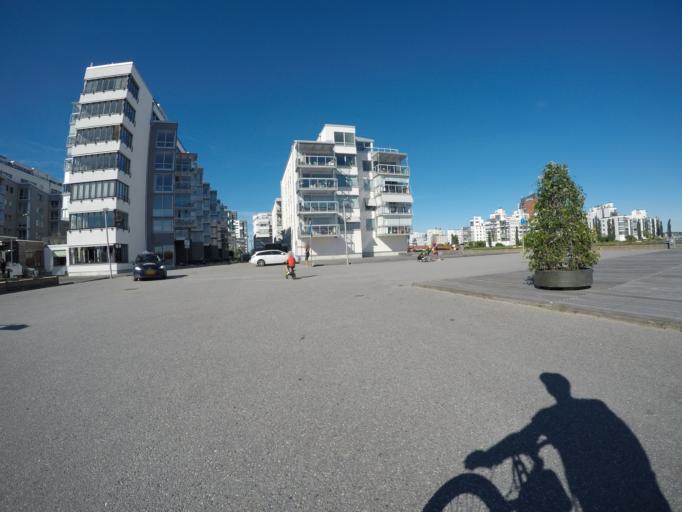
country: SE
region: Vaestmanland
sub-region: Vasteras
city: Vasteras
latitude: 59.6030
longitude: 16.5519
